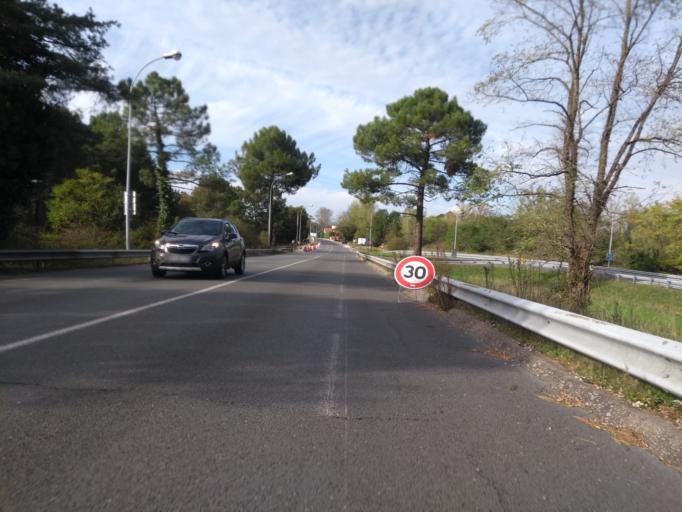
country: FR
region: Aquitaine
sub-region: Departement de la Gironde
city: Canejan
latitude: 44.7719
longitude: -0.6611
